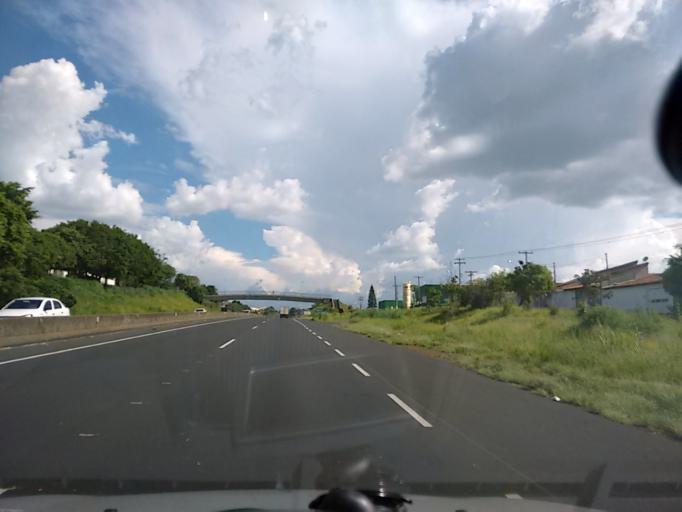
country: BR
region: Sao Paulo
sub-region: Marilia
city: Marilia
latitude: -22.1934
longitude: -49.9662
